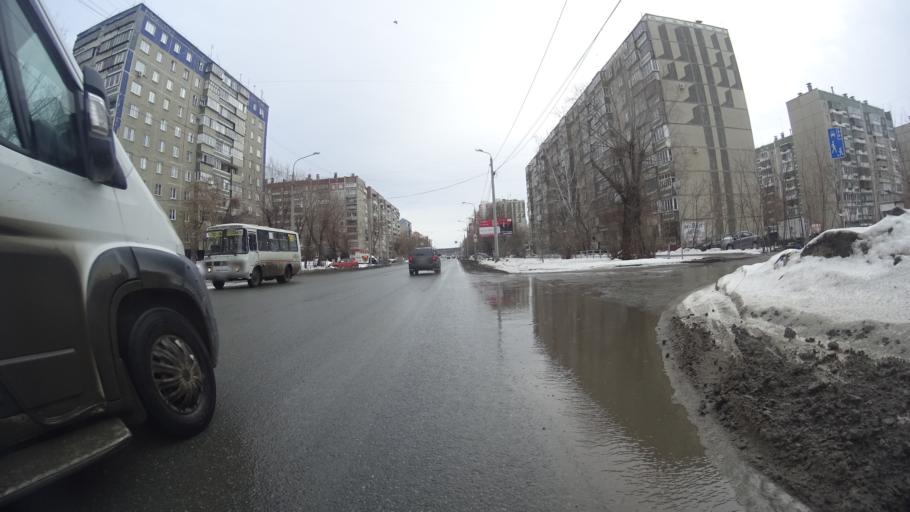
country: RU
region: Chelyabinsk
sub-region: Gorod Chelyabinsk
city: Chelyabinsk
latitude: 55.1796
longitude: 61.3076
